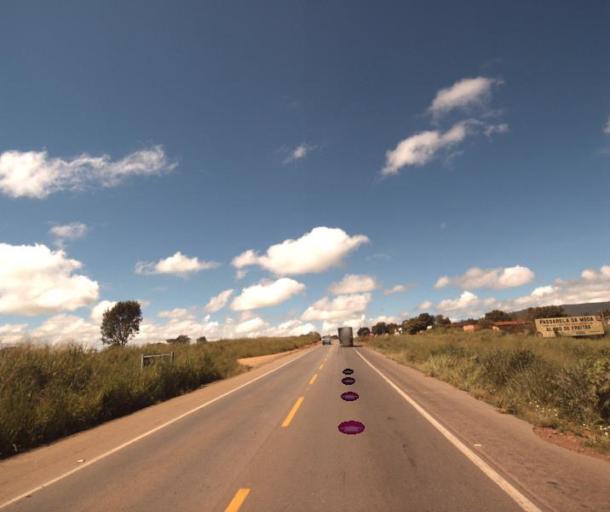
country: BR
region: Goias
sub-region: Jaragua
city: Jaragua
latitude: -15.7481
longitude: -49.3179
